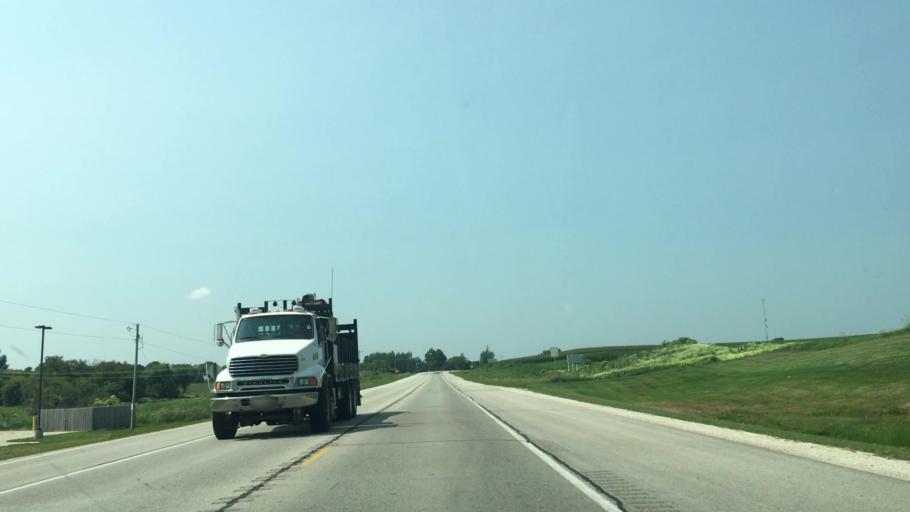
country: US
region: Iowa
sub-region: Winneshiek County
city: Decorah
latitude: 43.1912
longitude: -91.8675
